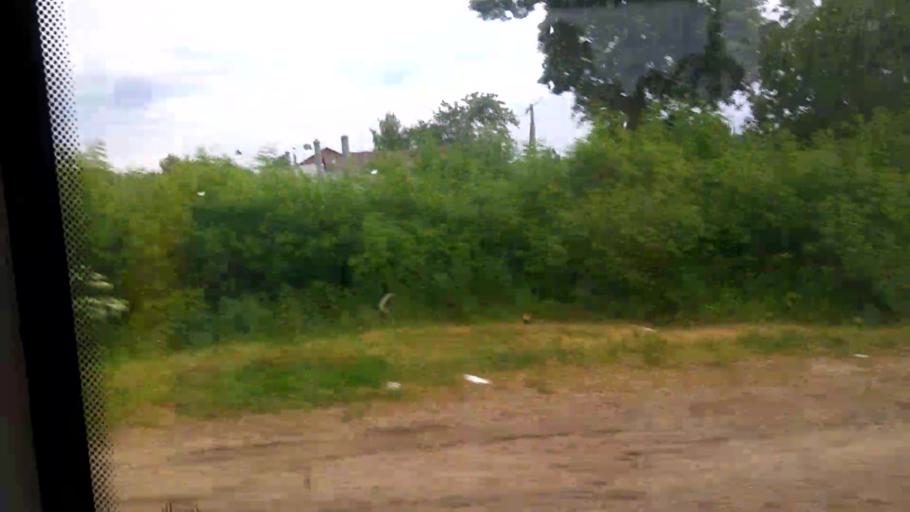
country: RU
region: Moskovskaya
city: Zaraysk
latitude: 54.7576
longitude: 38.8580
